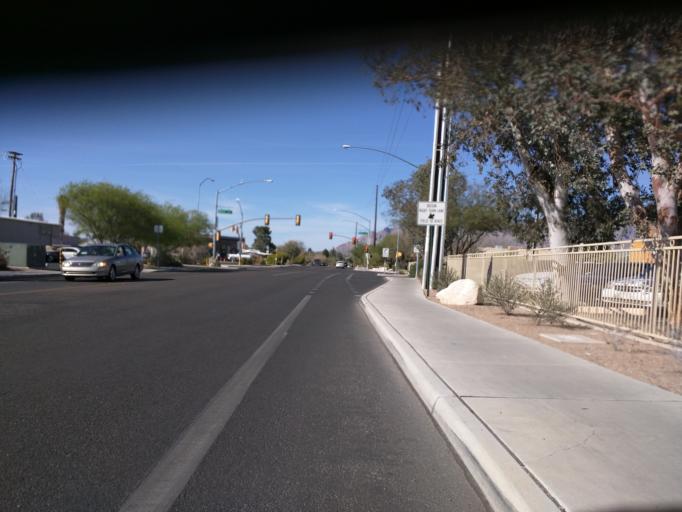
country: US
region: Arizona
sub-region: Pima County
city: Catalina Foothills
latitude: 32.2713
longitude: -110.9523
